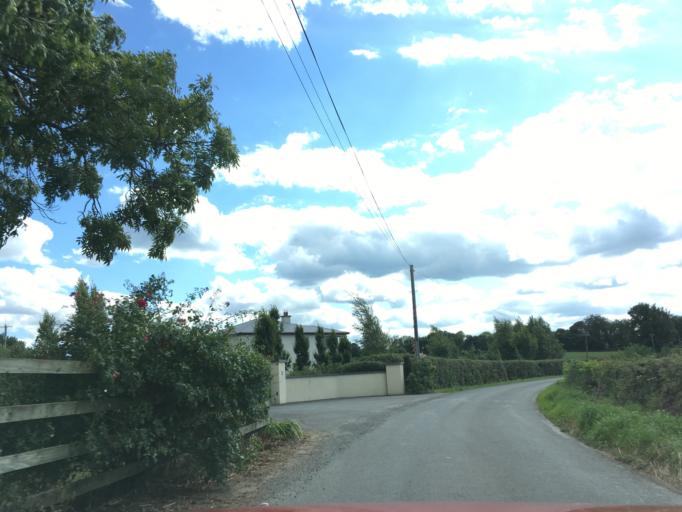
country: IE
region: Munster
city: Cashel
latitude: 52.4872
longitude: -7.9571
